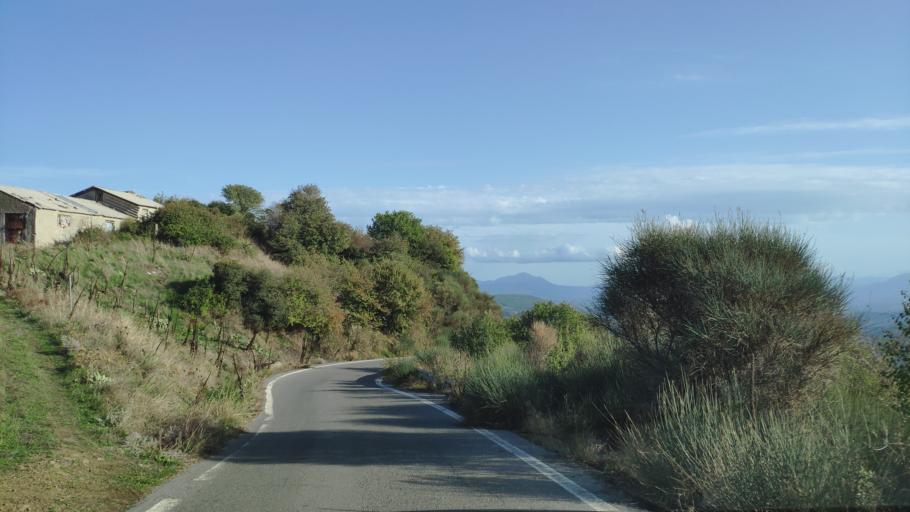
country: GR
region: Peloponnese
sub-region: Nomos Arkadias
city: Dimitsana
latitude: 37.5646
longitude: 22.0285
